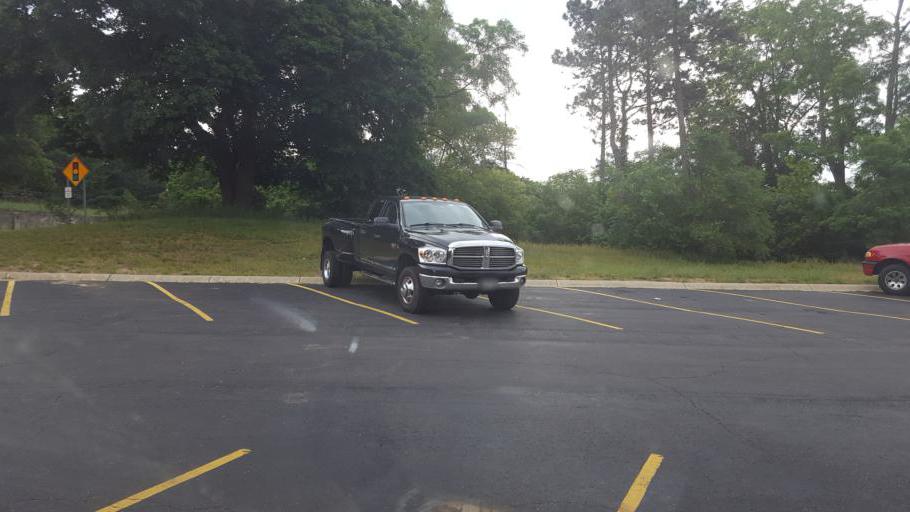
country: US
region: Michigan
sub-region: Eaton County
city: Charlotte
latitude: 42.5819
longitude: -84.8112
